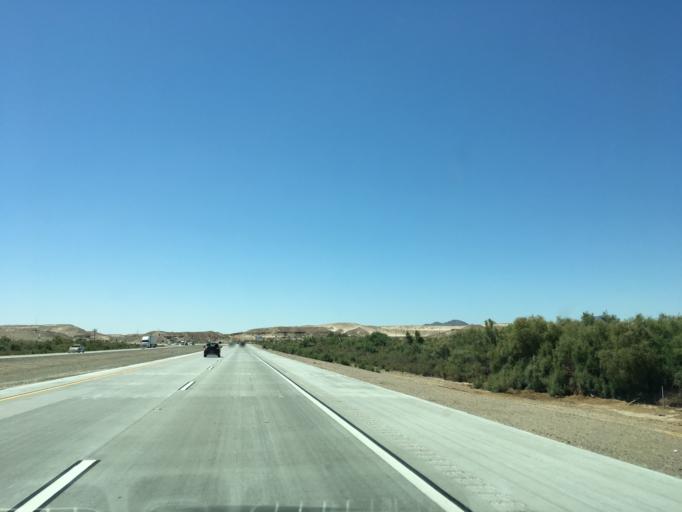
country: MX
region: Baja California
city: Los Algodones
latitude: 32.7444
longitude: -114.6905
